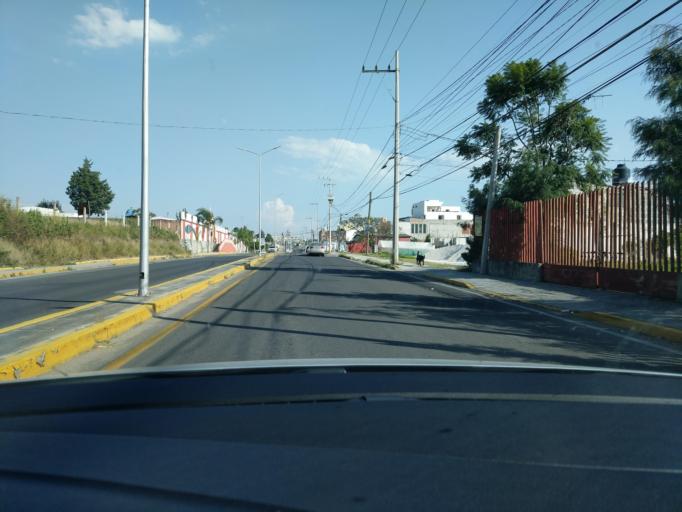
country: MX
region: Puebla
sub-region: San Gregorio Atzompa
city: Chipilo de Francisco Javier Mina
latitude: 19.0269
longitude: -98.3152
